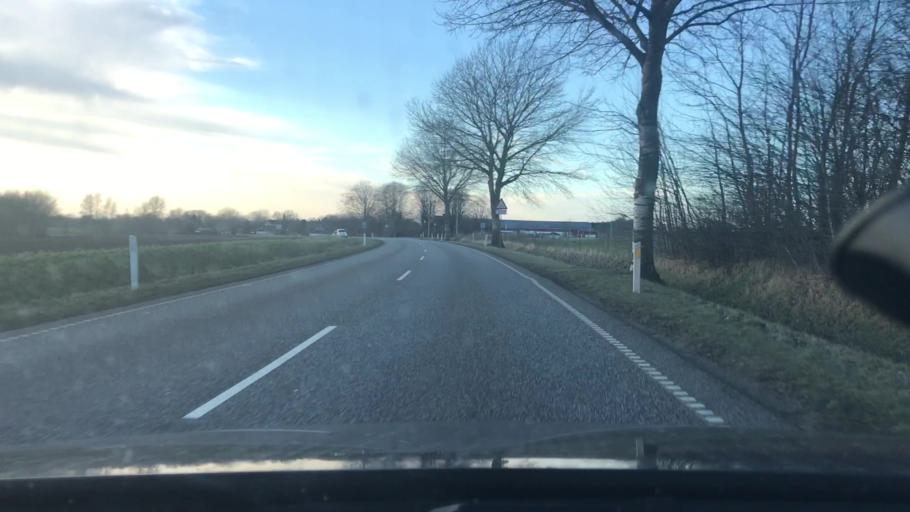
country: DK
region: Zealand
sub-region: Solrod Kommune
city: Solrod
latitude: 55.5167
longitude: 12.1576
